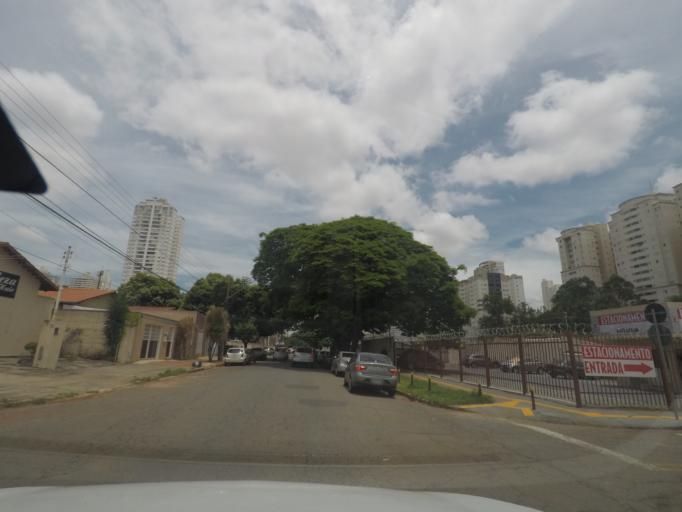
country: BR
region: Goias
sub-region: Goiania
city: Goiania
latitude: -16.6936
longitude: -49.2749
